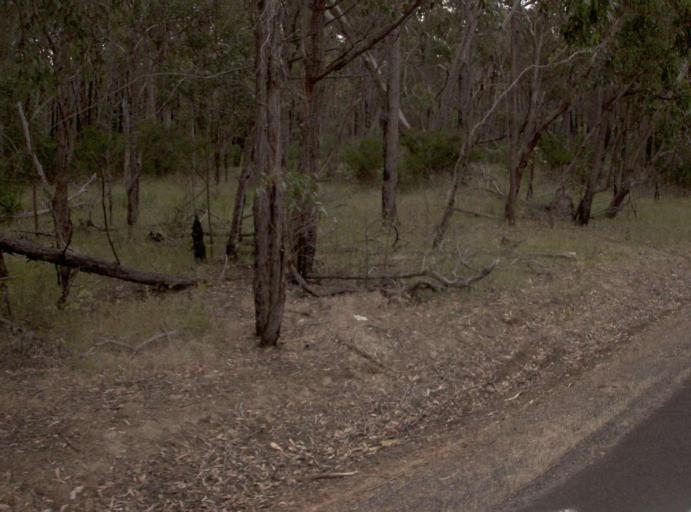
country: AU
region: Victoria
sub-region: Wellington
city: Sale
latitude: -38.4282
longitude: 146.9536
